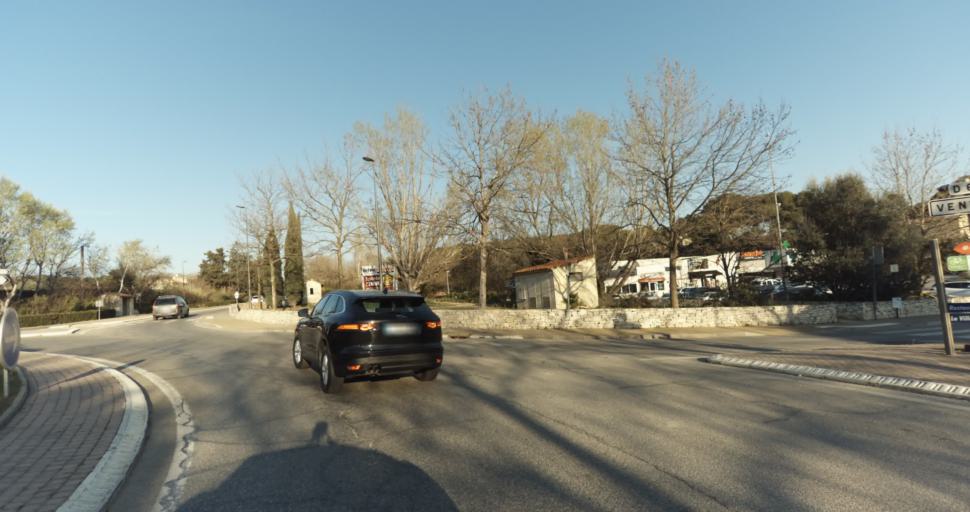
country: FR
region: Provence-Alpes-Cote d'Azur
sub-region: Departement des Bouches-du-Rhone
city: Ventabren
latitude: 43.5470
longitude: 5.2934
